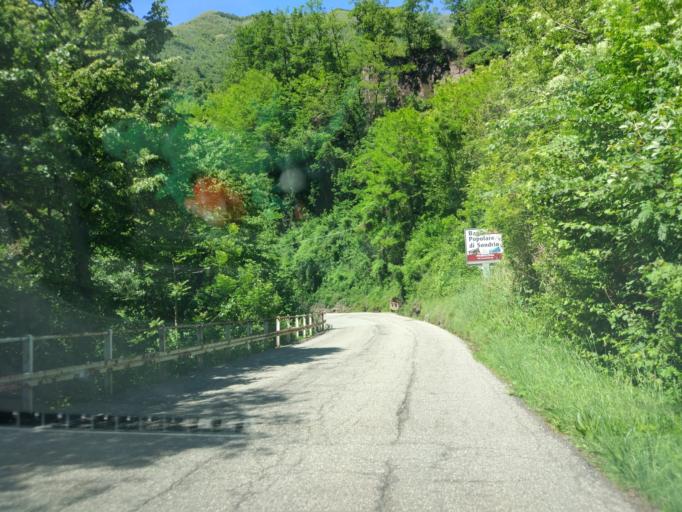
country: IT
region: Lombardy
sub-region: Provincia di Lecco
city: Taceno
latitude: 46.0239
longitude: 9.3682
